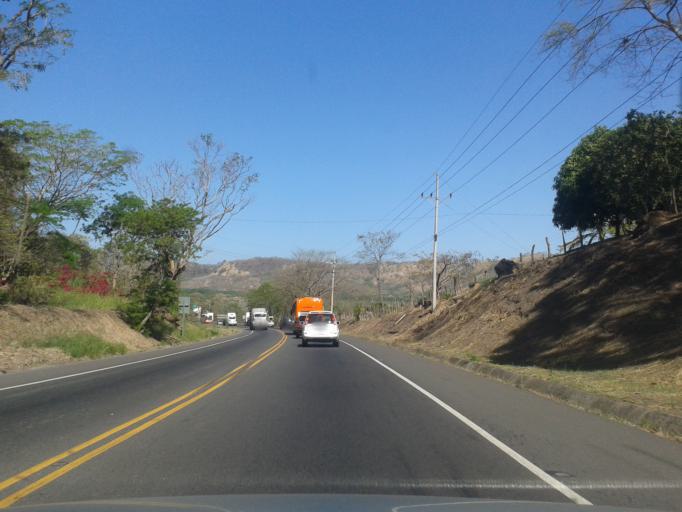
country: CR
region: Puntarenas
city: Esparza
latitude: 9.9189
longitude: -84.6853
